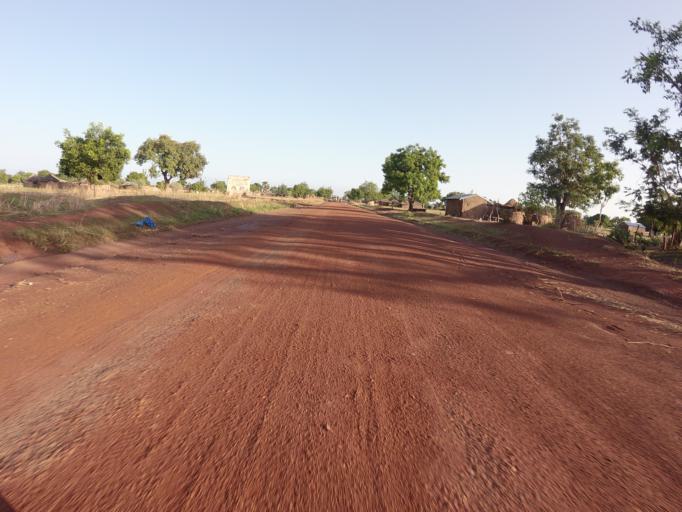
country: TG
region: Savanes
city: Sansanne-Mango
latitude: 10.3579
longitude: -0.0933
